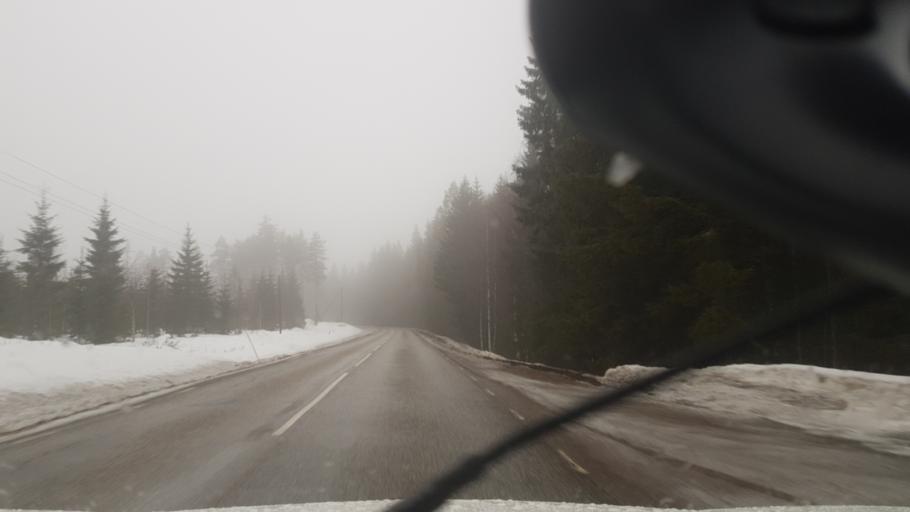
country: SE
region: Vaermland
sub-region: Arjangs Kommun
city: Arjaeng
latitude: 59.5779
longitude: 12.2482
